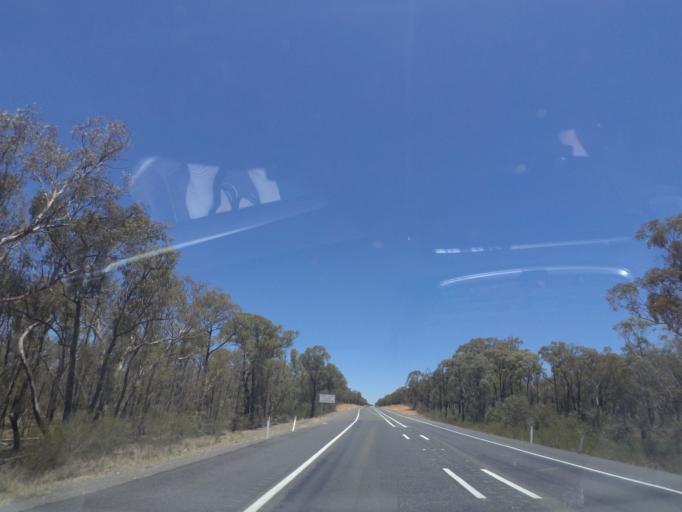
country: AU
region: New South Wales
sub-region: Warrumbungle Shire
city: Coonabarabran
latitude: -30.8929
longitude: 149.4418
